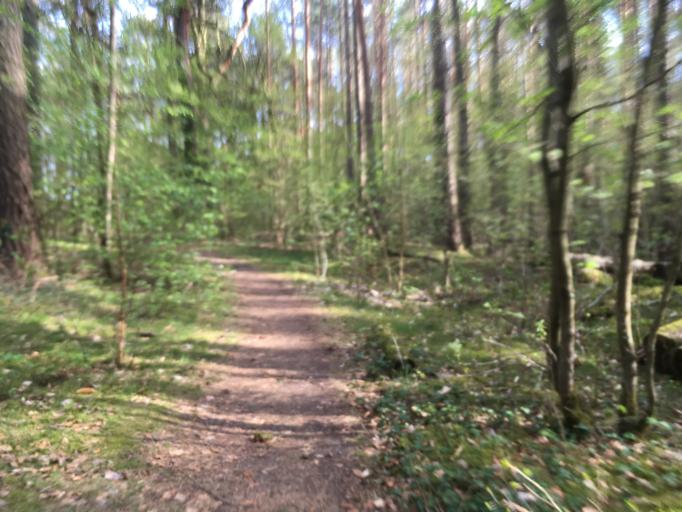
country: DE
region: Brandenburg
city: Bernau bei Berlin
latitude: 52.7055
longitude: 13.5792
